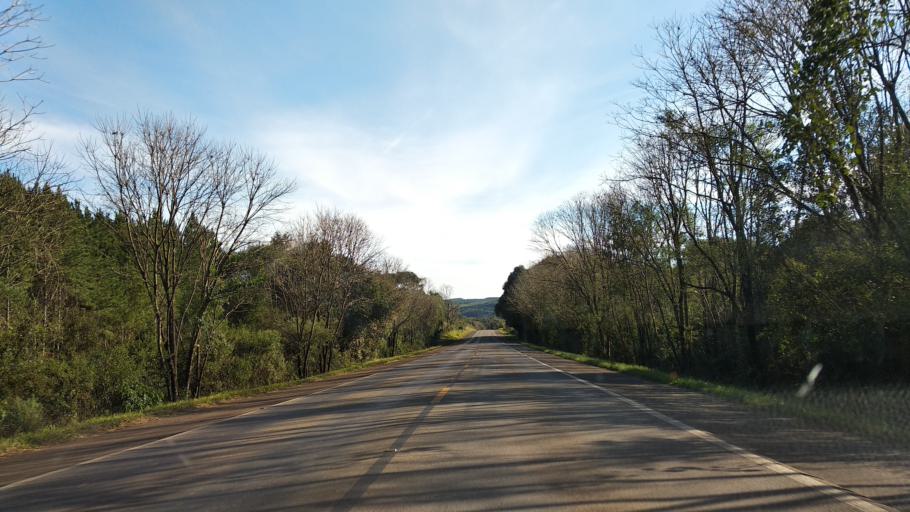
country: BR
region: Santa Catarina
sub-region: Celso Ramos
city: Celso Ramos
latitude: -27.5453
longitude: -51.4272
